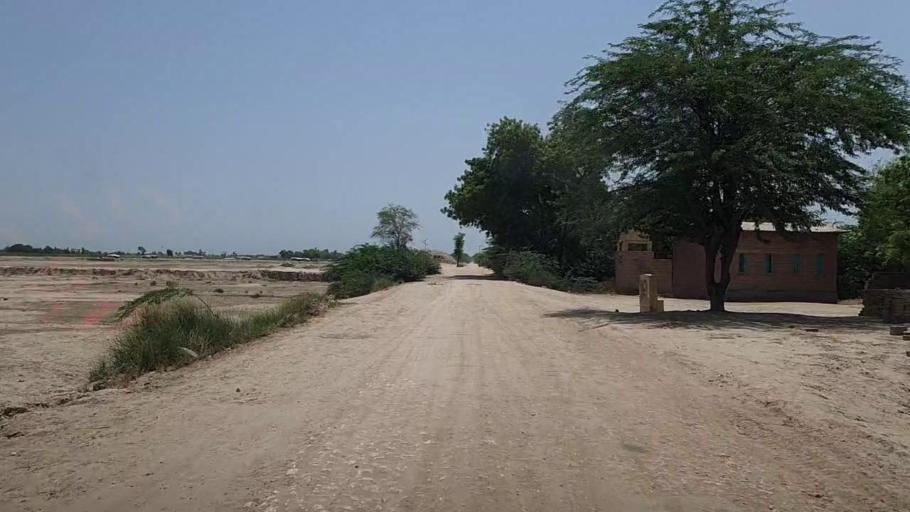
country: PK
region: Sindh
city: Pad Idan
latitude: 26.7657
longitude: 68.2936
